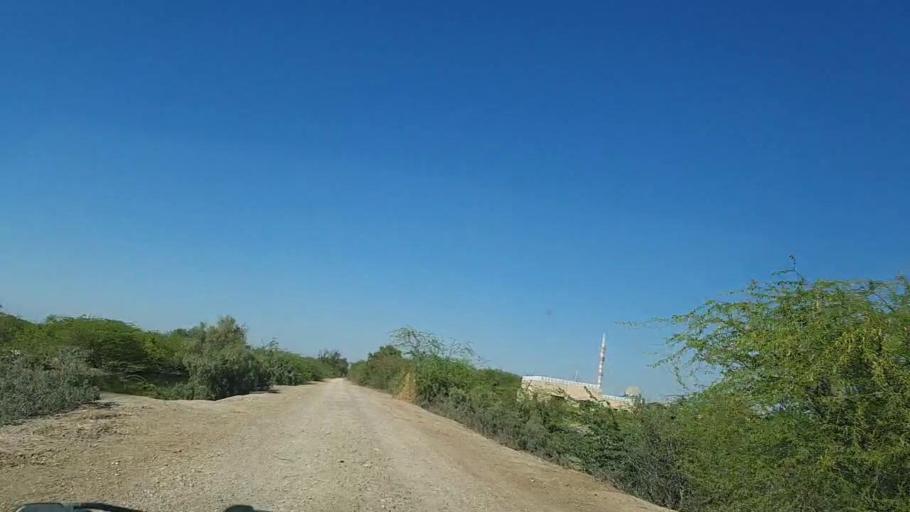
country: PK
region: Sindh
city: Dhoro Naro
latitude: 25.5305
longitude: 69.4797
